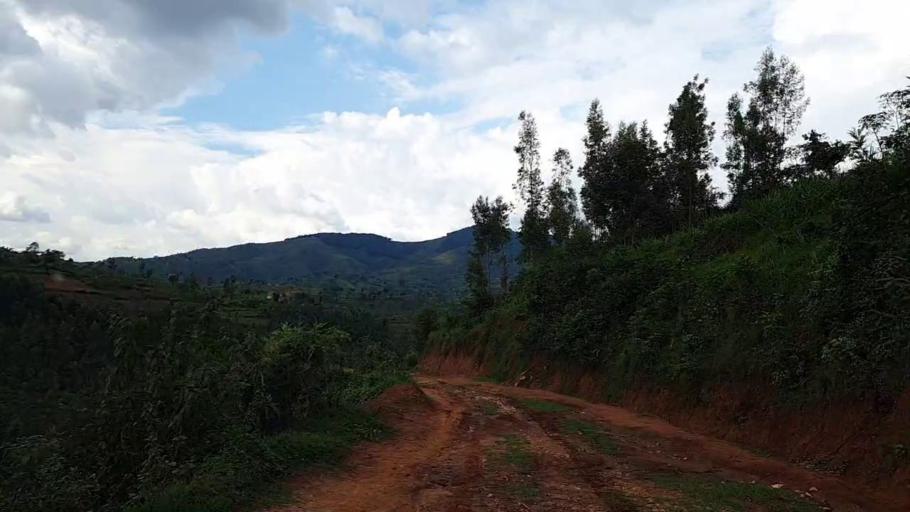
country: RW
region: Southern Province
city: Gikongoro
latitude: -2.4201
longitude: 29.6540
